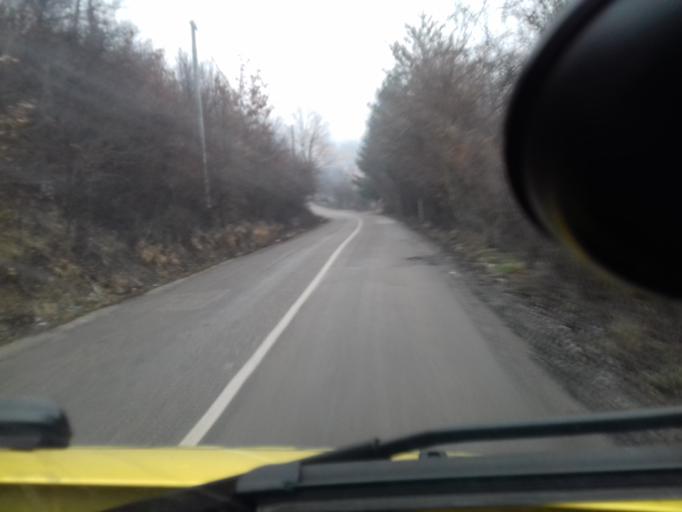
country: BA
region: Federation of Bosnia and Herzegovina
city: Lokvine
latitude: 44.2008
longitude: 17.8655
